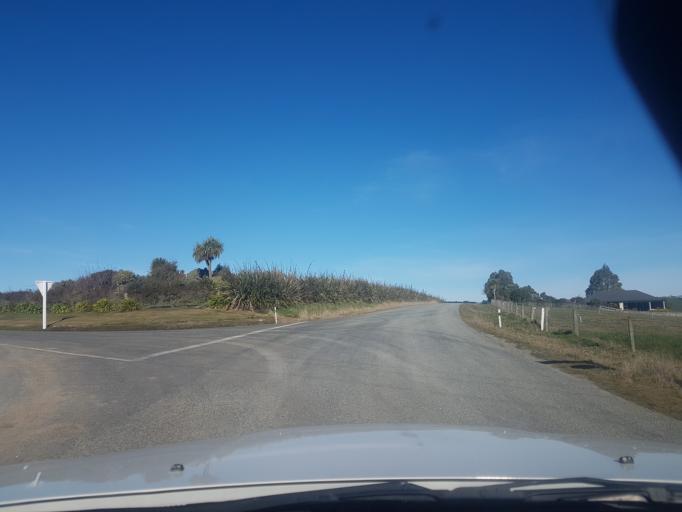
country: NZ
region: Canterbury
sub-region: Timaru District
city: Pleasant Point
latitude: -44.3596
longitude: 171.0698
